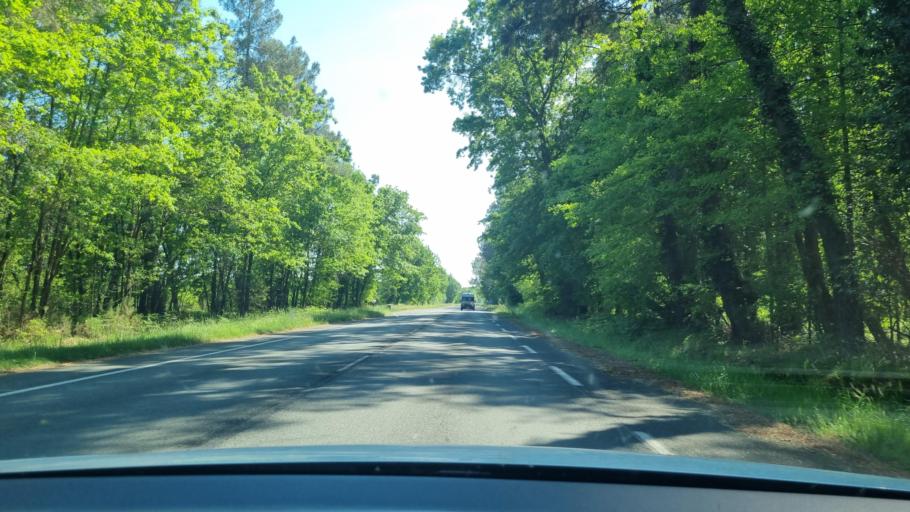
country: FR
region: Aquitaine
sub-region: Departement des Landes
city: Roquefort
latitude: 44.1976
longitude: -0.2710
